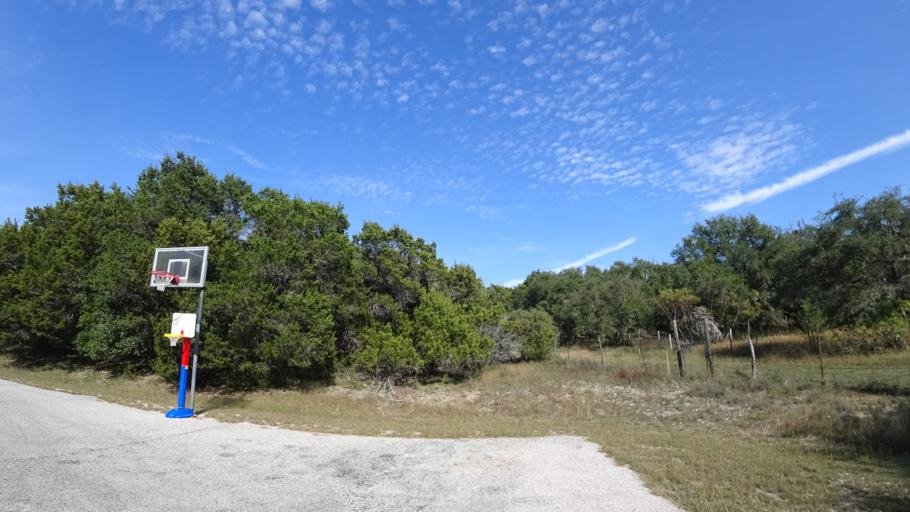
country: US
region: Texas
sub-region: Travis County
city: Barton Creek
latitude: 30.2260
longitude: -97.9179
